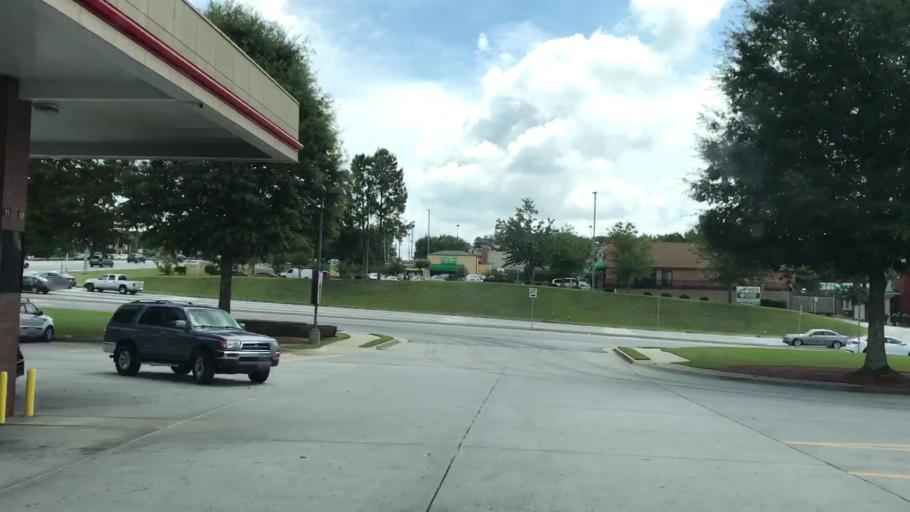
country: US
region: Georgia
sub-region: Gwinnett County
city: Buford
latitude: 34.0892
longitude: -83.9978
